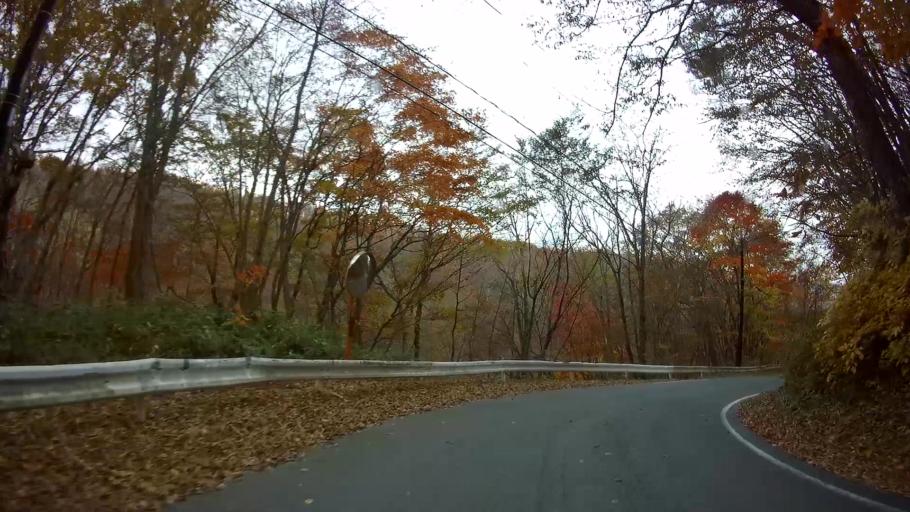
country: JP
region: Gunma
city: Nakanojomachi
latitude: 36.6654
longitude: 138.6696
